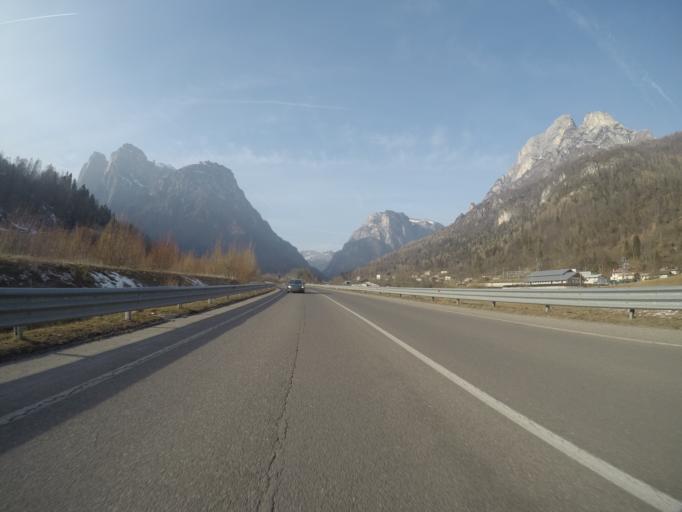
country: IT
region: Veneto
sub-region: Provincia di Belluno
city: Taibon Agordino
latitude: 46.2899
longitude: 12.0222
